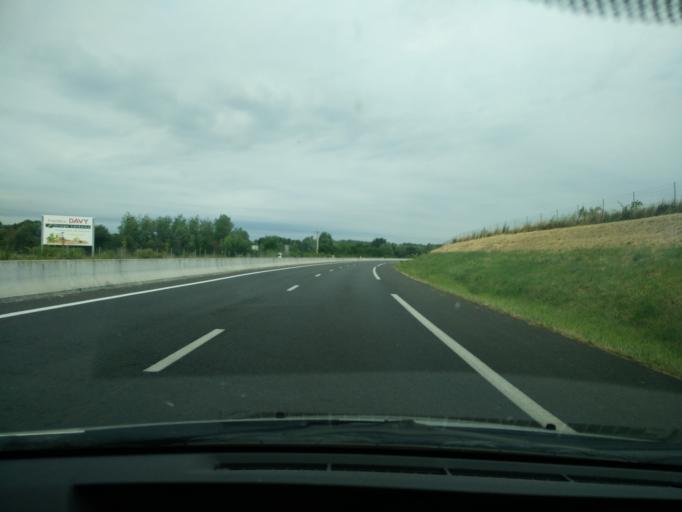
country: FR
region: Pays de la Loire
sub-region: Departement de Maine-et-Loire
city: Saint-Jean
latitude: 47.2936
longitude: -0.3878
